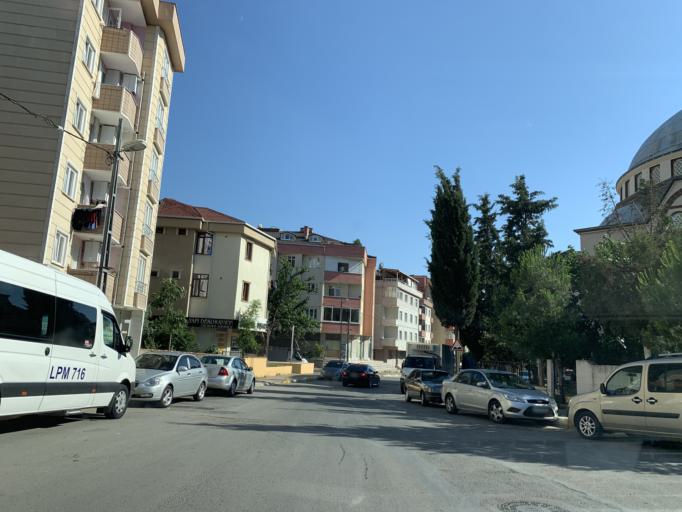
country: TR
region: Istanbul
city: Pendik
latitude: 40.8884
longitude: 29.2687
